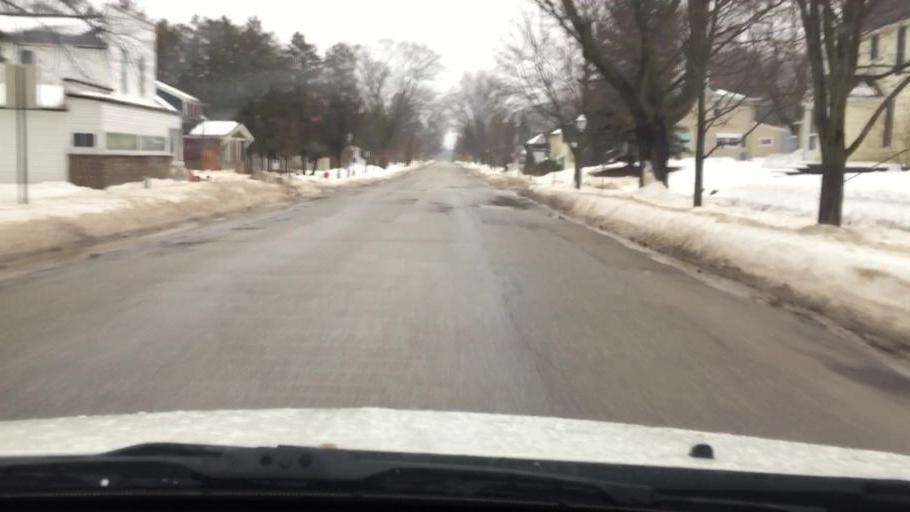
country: US
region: Michigan
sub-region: Charlevoix County
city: Charlevoix
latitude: 45.3153
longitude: -85.2676
